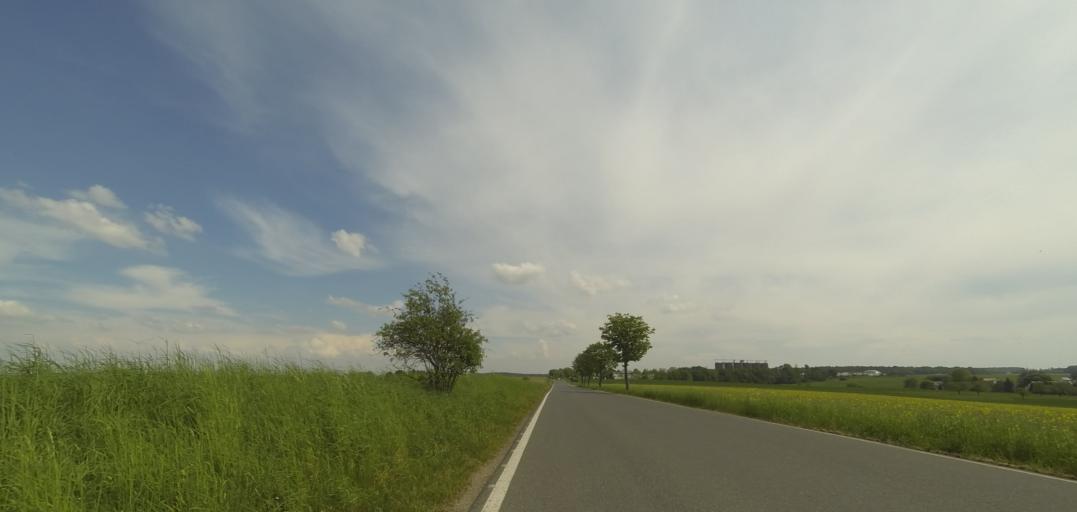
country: DE
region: Saxony
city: Radeberg
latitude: 51.0801
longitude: 13.9249
